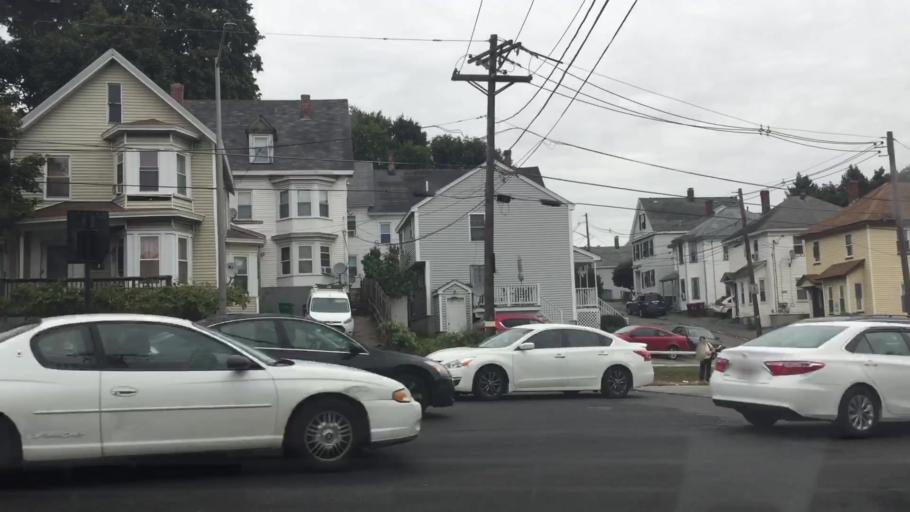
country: US
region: Massachusetts
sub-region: Middlesex County
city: Lowell
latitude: 42.6350
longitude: -71.3118
